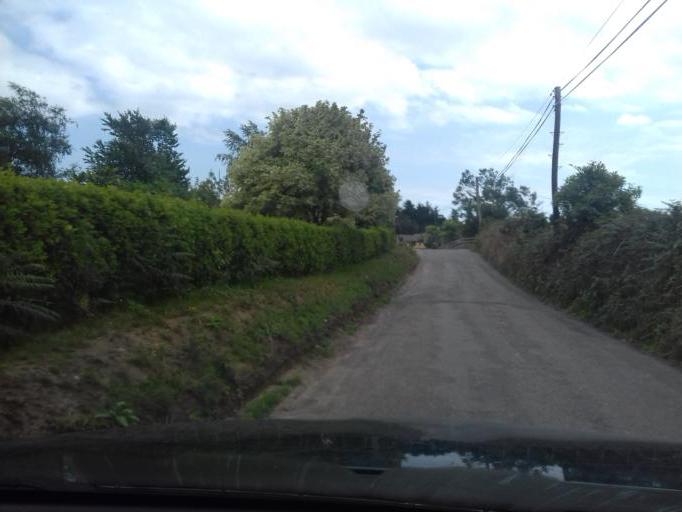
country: IE
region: Leinster
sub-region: Loch Garman
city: Castlebridge
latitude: 52.4018
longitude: -6.4022
